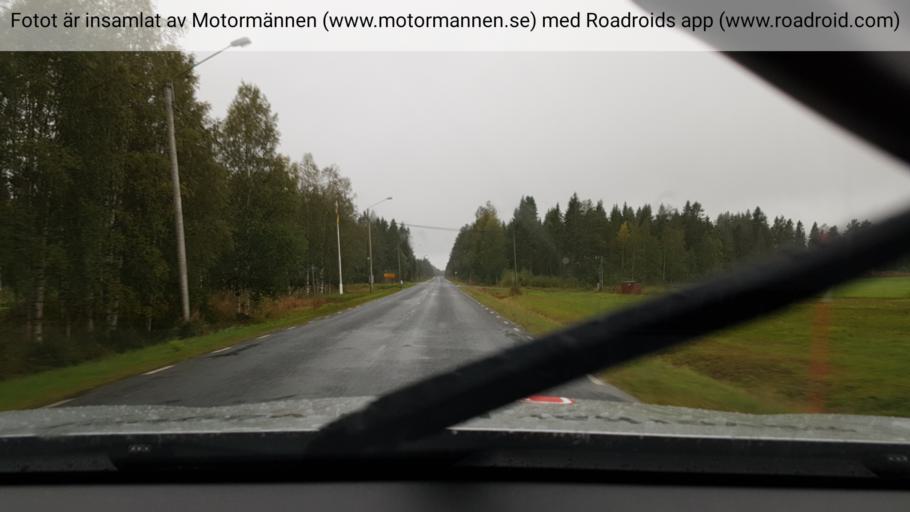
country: SE
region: Vaesterbotten
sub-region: Skelleftea Kommun
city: Storvik
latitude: 64.9724
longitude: 20.6892
